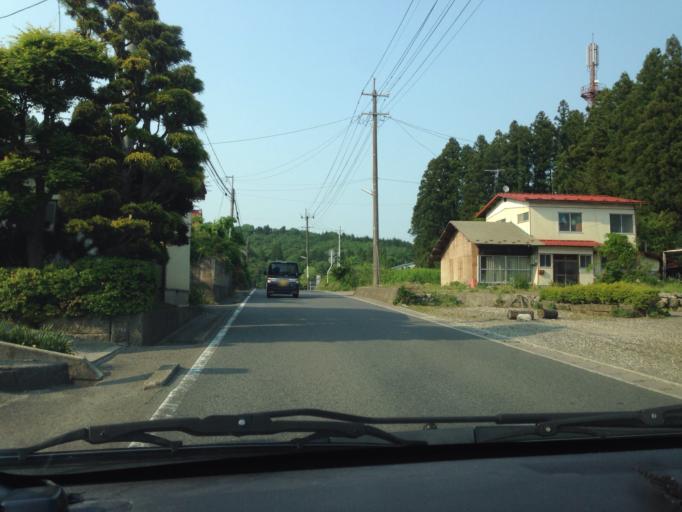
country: JP
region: Tochigi
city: Kuroiso
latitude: 37.0804
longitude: 140.1917
